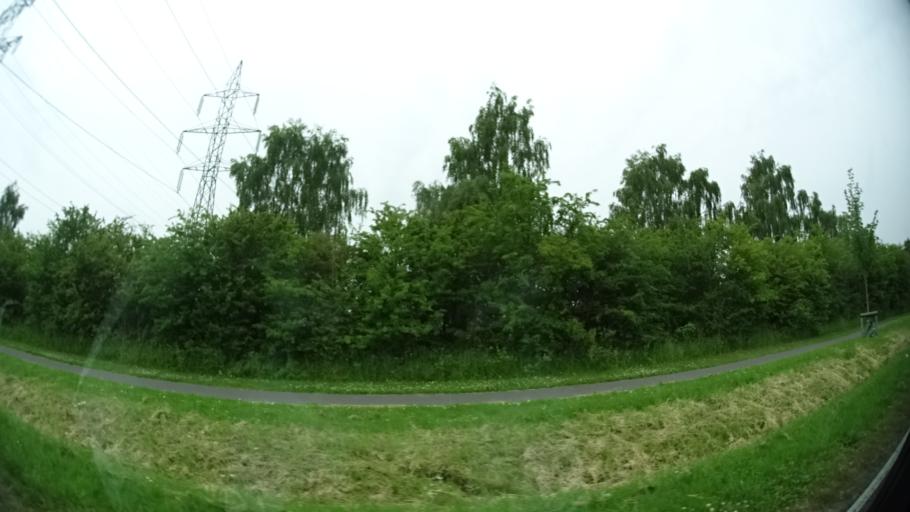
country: DK
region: Central Jutland
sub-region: Arhus Kommune
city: Logten
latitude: 56.2538
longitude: 10.3030
